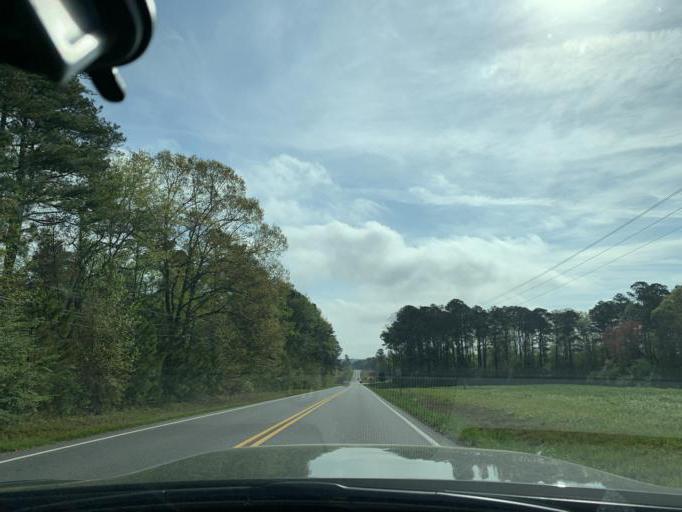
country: US
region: Georgia
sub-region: Forsyth County
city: Cumming
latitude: 34.2500
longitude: -84.1082
